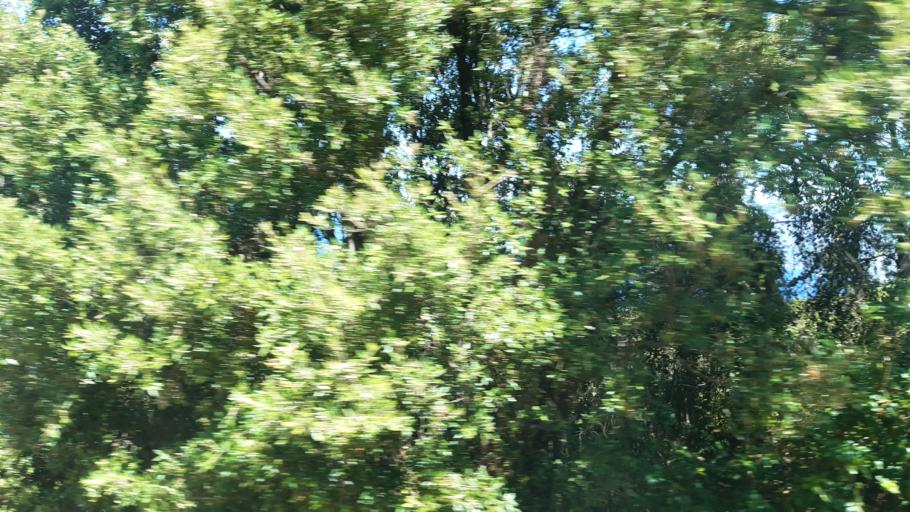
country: FR
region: Corsica
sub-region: Departement de la Corse-du-Sud
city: Cargese
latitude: 42.2437
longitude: 8.6204
